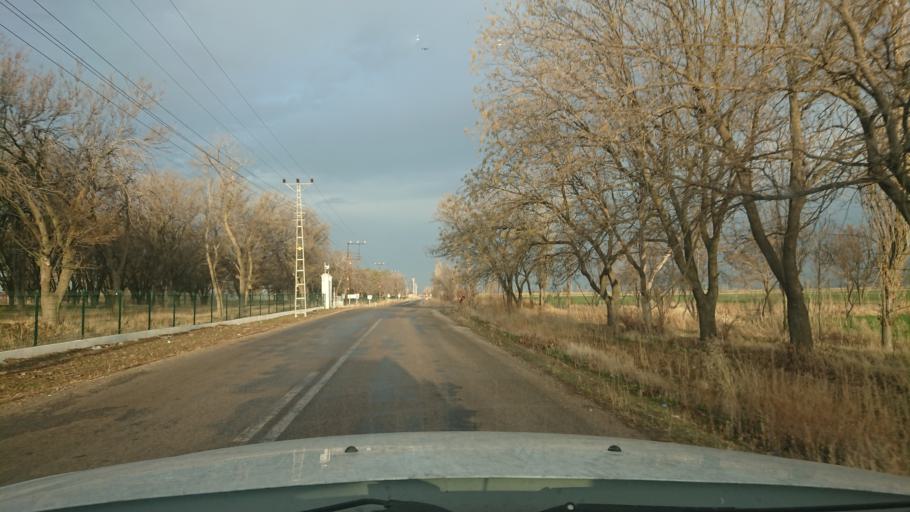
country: TR
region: Aksaray
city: Yesilova
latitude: 38.4612
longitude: 33.8415
